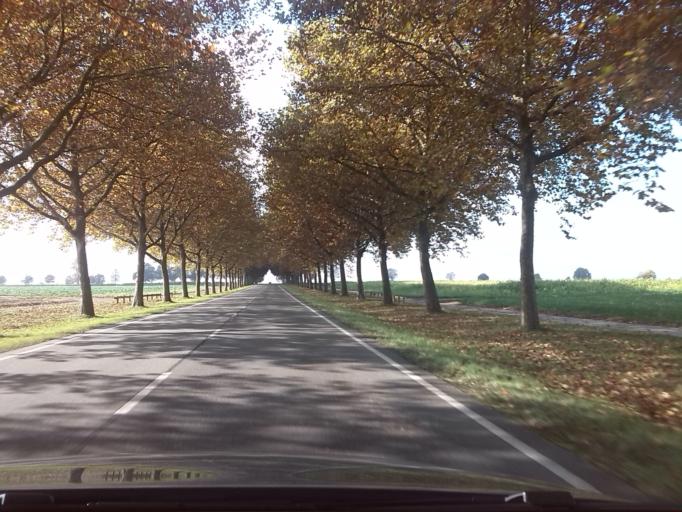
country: DE
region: Baden-Wuerttemberg
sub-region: Regierungsbezirk Stuttgart
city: Fellbach
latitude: 48.8239
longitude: 9.2630
